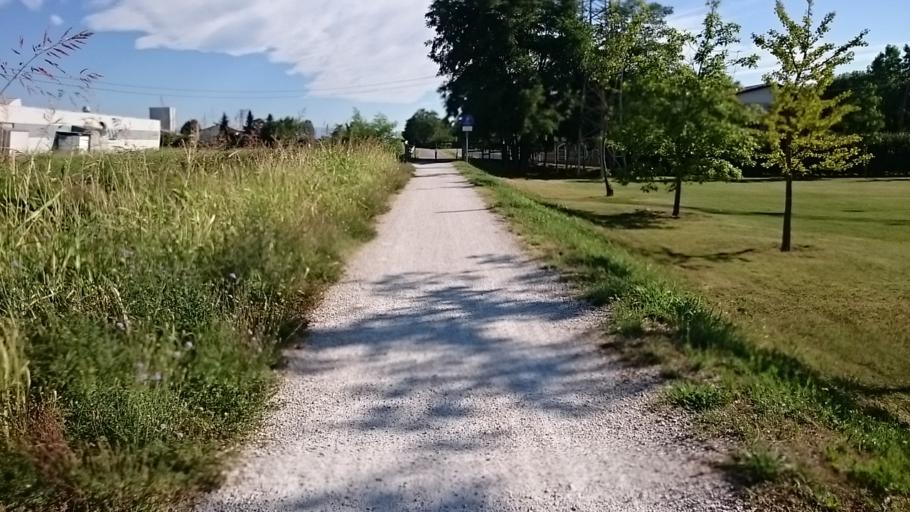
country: IT
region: Veneto
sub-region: Provincia di Padova
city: Camposampiero
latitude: 45.5500
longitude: 11.9314
